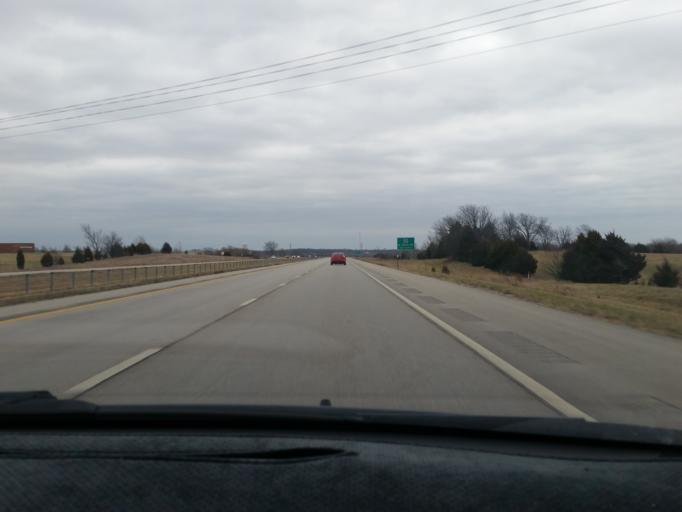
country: US
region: Kansas
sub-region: Douglas County
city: Eudora
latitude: 38.9345
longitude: -95.0844
